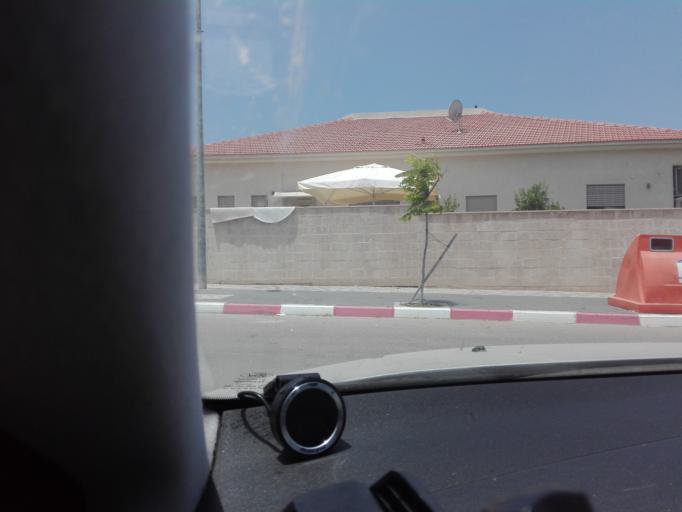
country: IL
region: Central District
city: Bene 'Ayish
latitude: 31.7403
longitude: 34.7436
